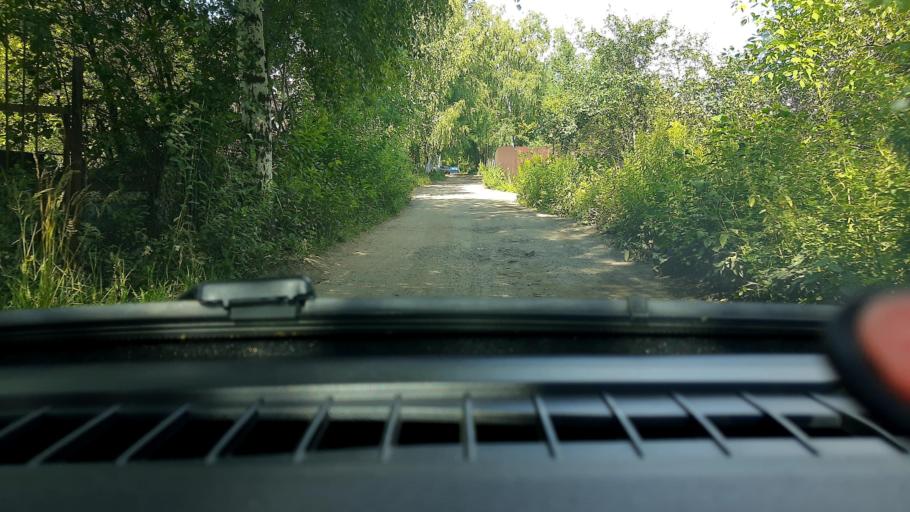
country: RU
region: Nizjnij Novgorod
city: Gorbatovka
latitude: 56.3232
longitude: 43.8306
